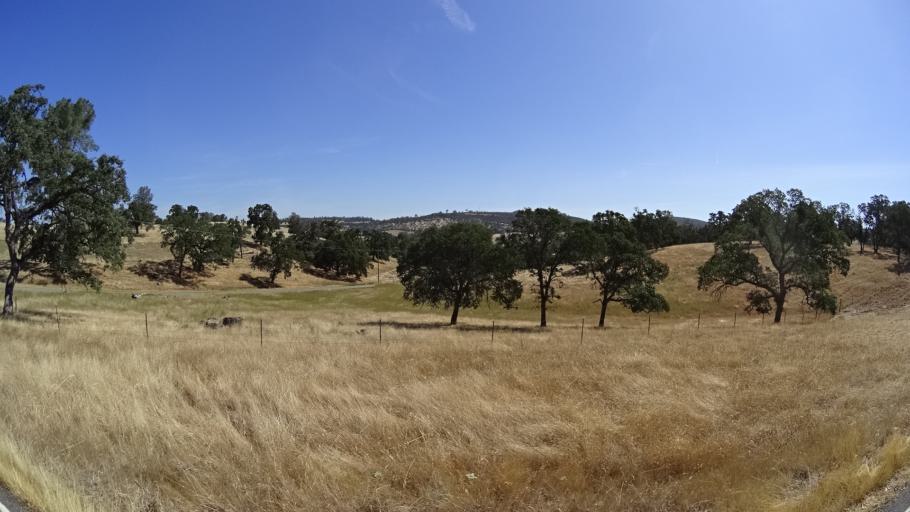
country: US
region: California
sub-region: Calaveras County
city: Valley Springs
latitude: 38.2292
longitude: -120.8302
